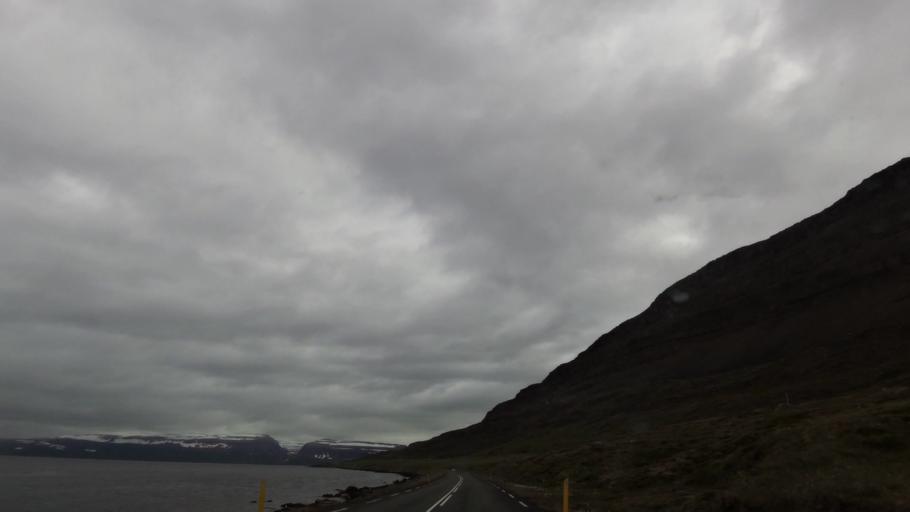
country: IS
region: Westfjords
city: Isafjoerdur
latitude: 66.0261
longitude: -22.7791
